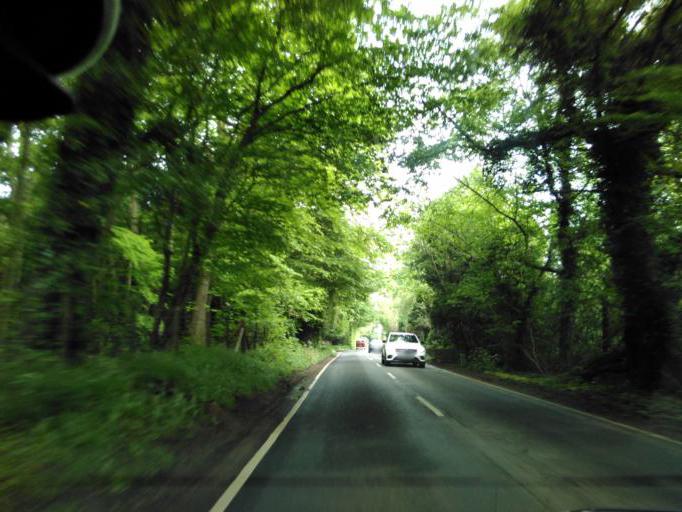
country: GB
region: England
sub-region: Kent
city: Lyminge
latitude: 51.1919
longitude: 1.0552
